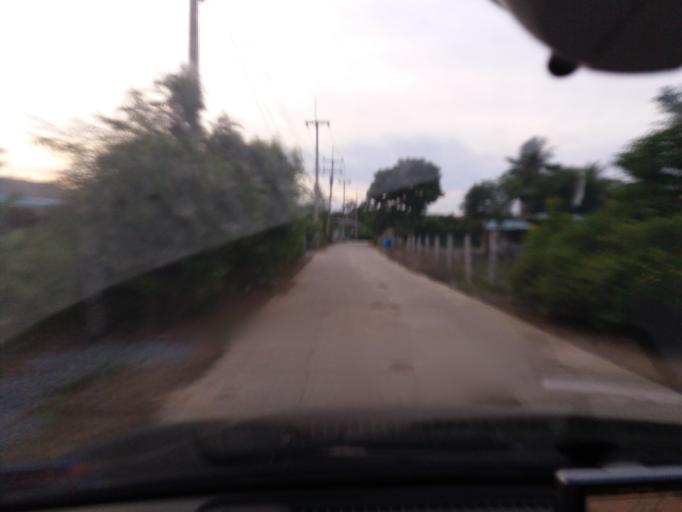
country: TH
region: Suphan Buri
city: Doembang Nangbuat
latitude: 14.8298
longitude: 100.1361
